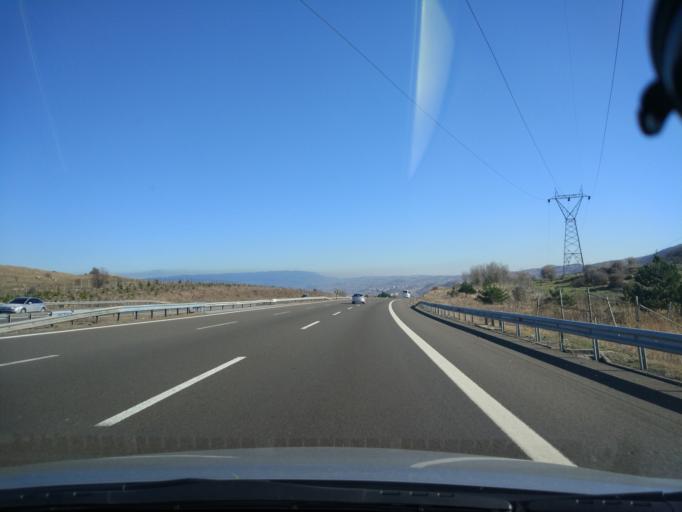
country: TR
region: Bolu
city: Yenicaga
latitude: 40.7614
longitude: 31.9803
